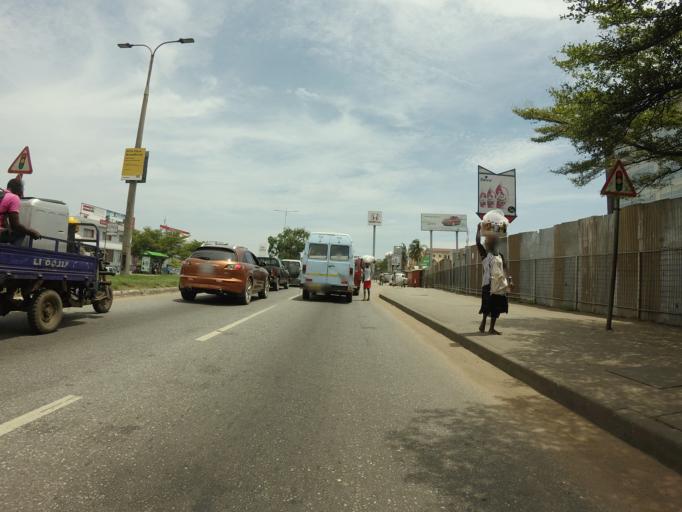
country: GH
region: Greater Accra
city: Accra
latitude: 5.5580
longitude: -0.2240
